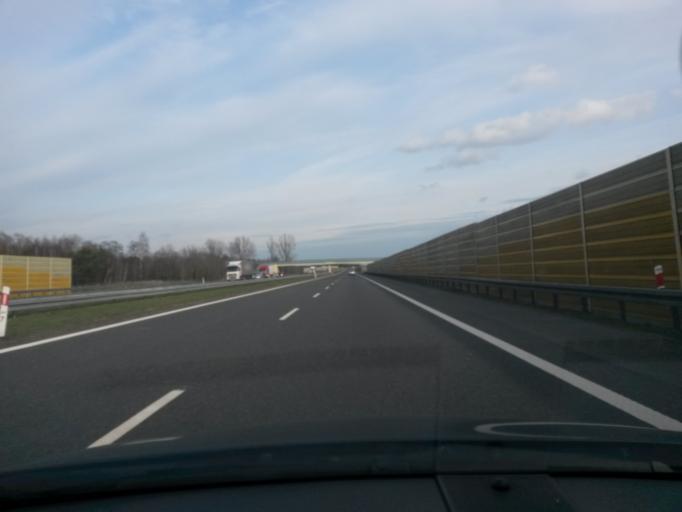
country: PL
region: Lodz Voivodeship
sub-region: Powiat leczycki
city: Swinice Warckie
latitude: 52.0290
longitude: 18.9018
